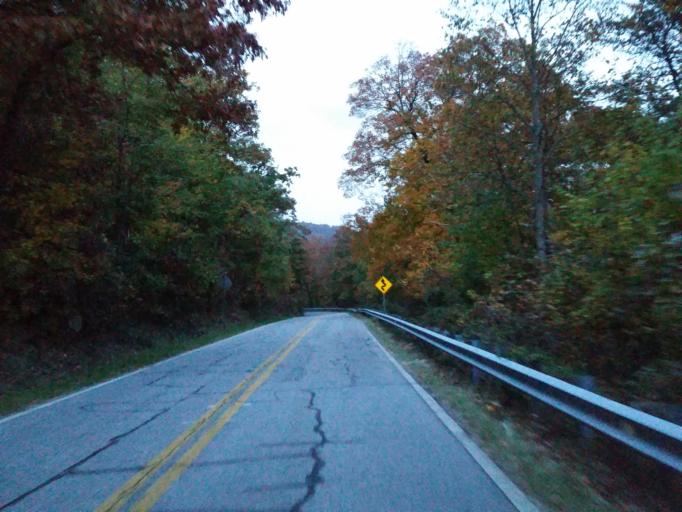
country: US
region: Georgia
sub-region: Lumpkin County
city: Dahlonega
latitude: 34.6611
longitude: -83.9780
